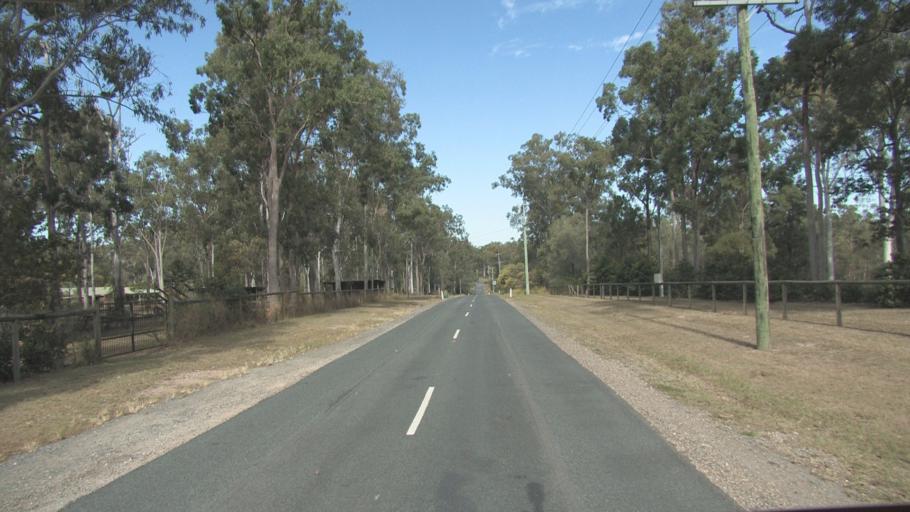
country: AU
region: Queensland
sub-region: Logan
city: North Maclean
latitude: -27.7476
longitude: 152.9737
